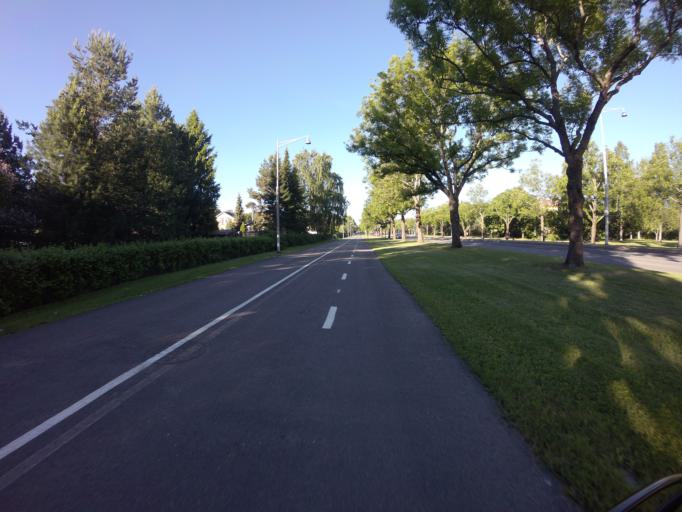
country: FI
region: Varsinais-Suomi
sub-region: Turku
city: Turku
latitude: 60.4681
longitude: 22.2780
